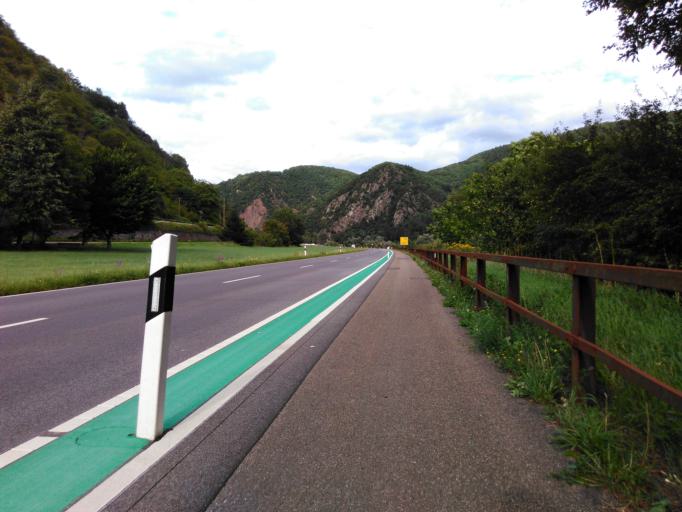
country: DE
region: Rheinland-Pfalz
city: Moselkern
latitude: 50.1870
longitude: 7.3604
